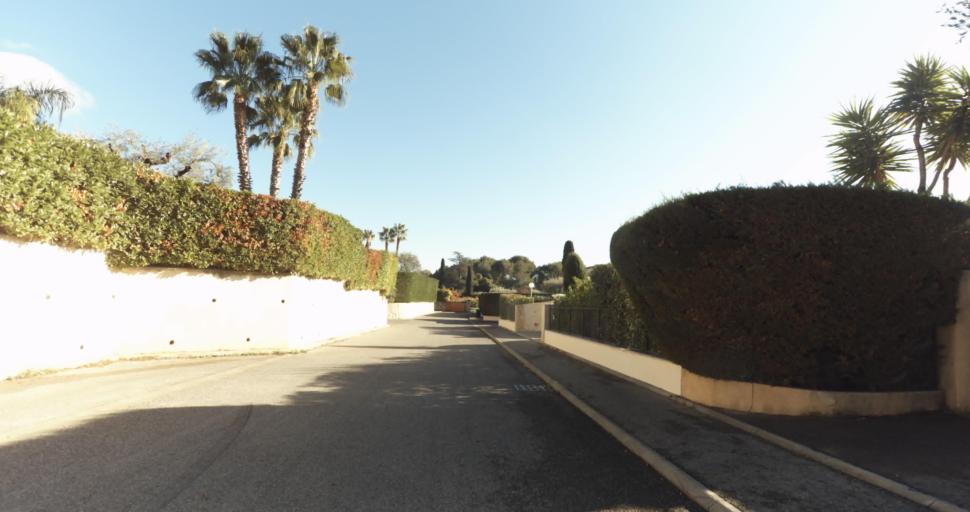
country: FR
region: Provence-Alpes-Cote d'Azur
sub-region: Departement des Alpes-Maritimes
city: La Gaude
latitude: 43.7120
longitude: 7.1359
